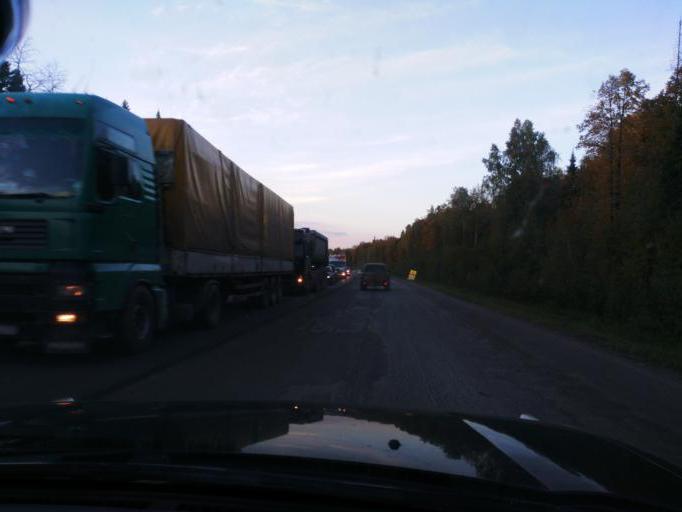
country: RU
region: Perm
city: Novyye Lyady
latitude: 58.0702
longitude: 56.4314
